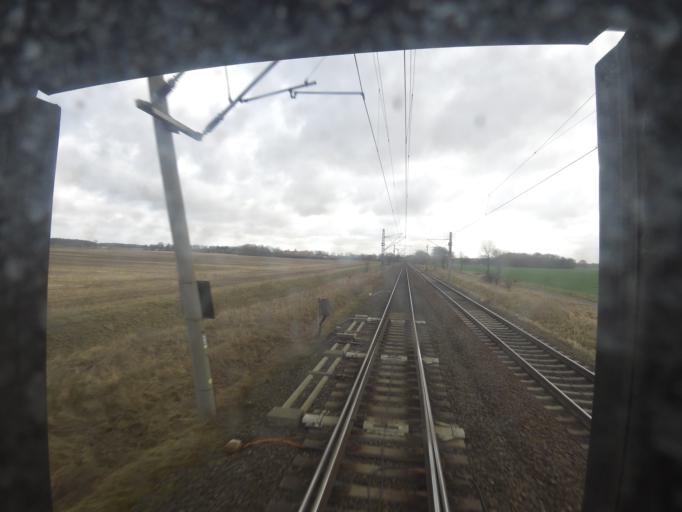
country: DE
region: Mecklenburg-Vorpommern
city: Lubtheen
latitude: 53.3615
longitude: 10.9653
